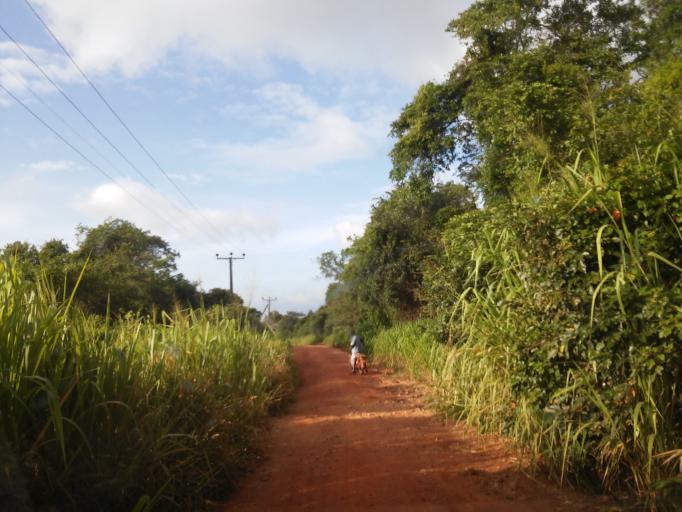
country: LK
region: Central
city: Sigiriya
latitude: 8.1684
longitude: 80.6849
